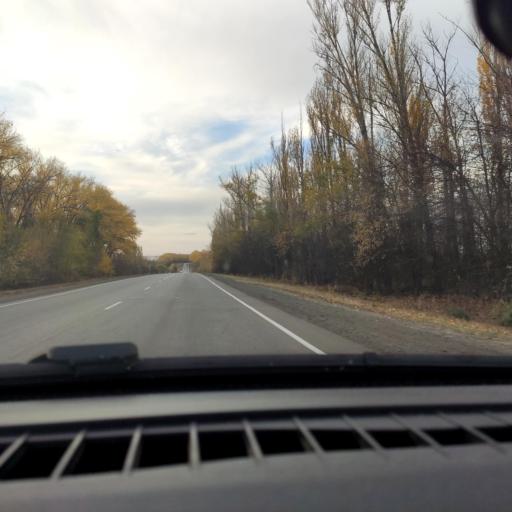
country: RU
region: Voronezj
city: Ostrogozhsk
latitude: 50.9676
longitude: 39.0090
